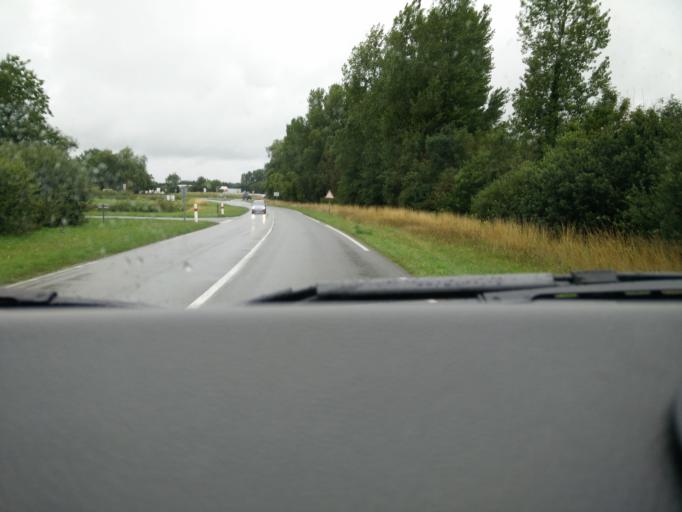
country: FR
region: Picardie
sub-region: Departement de la Somme
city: Rue
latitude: 50.2591
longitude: 1.6669
